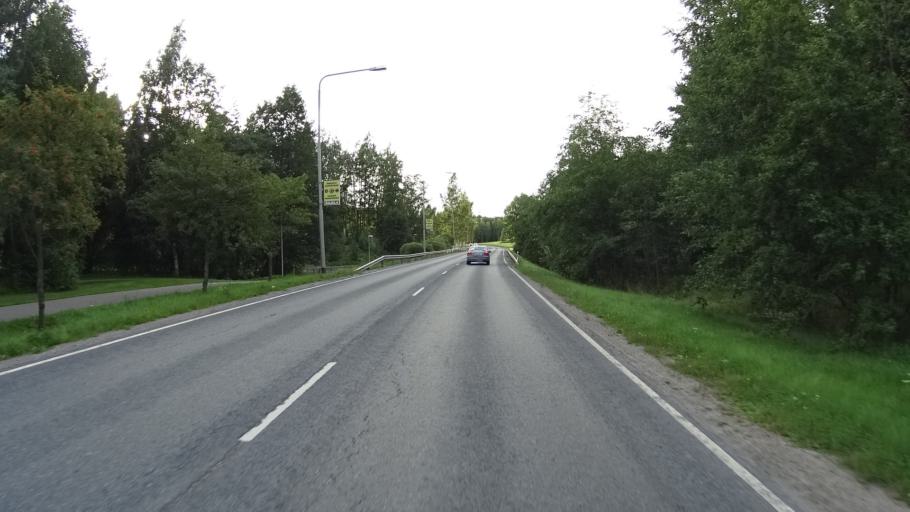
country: FI
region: Uusimaa
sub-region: Helsinki
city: Vantaa
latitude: 60.3036
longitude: 25.0175
